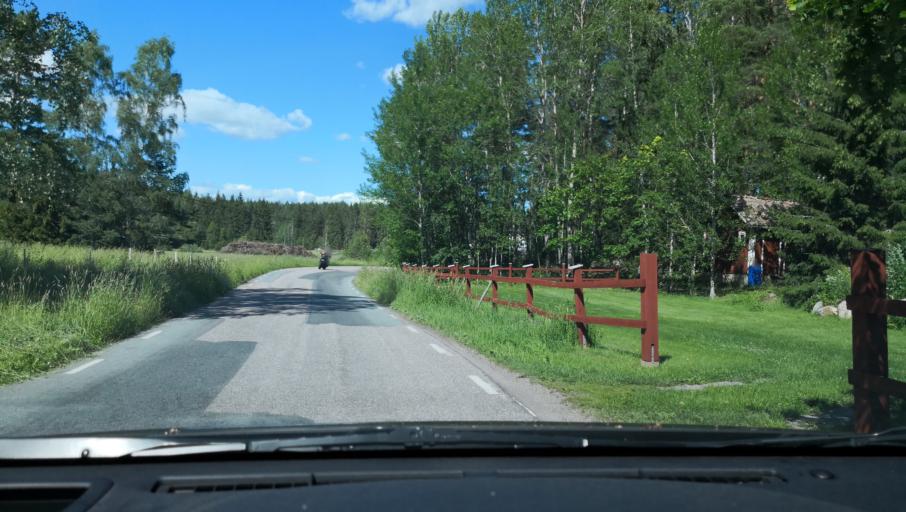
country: SE
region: Soedermanland
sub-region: Eskilstuna Kommun
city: Hallbybrunn
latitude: 59.3129
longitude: 16.3773
